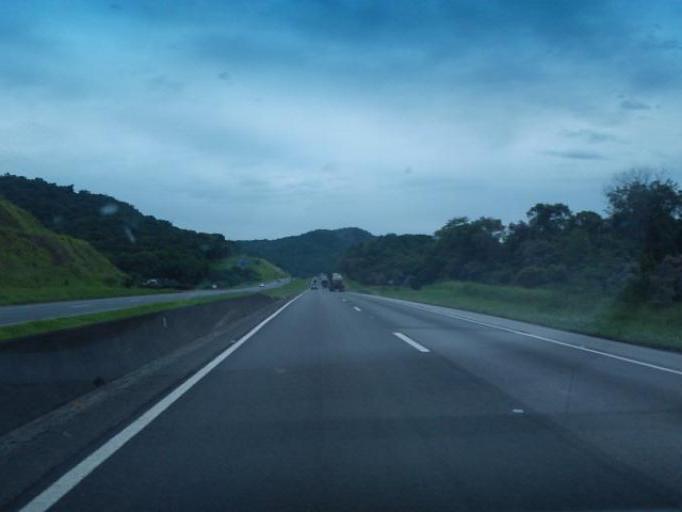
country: BR
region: Sao Paulo
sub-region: Juquia
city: Juquia
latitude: -24.3505
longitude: -47.6545
